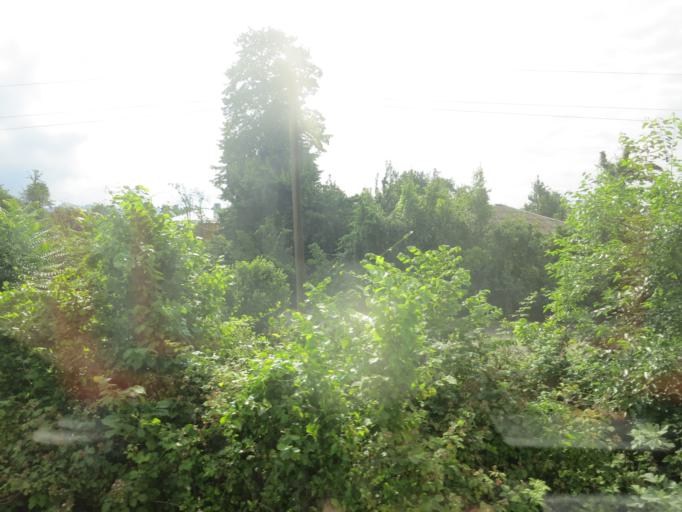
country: GE
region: Guria
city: Urek'i
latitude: 42.0375
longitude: 41.8128
